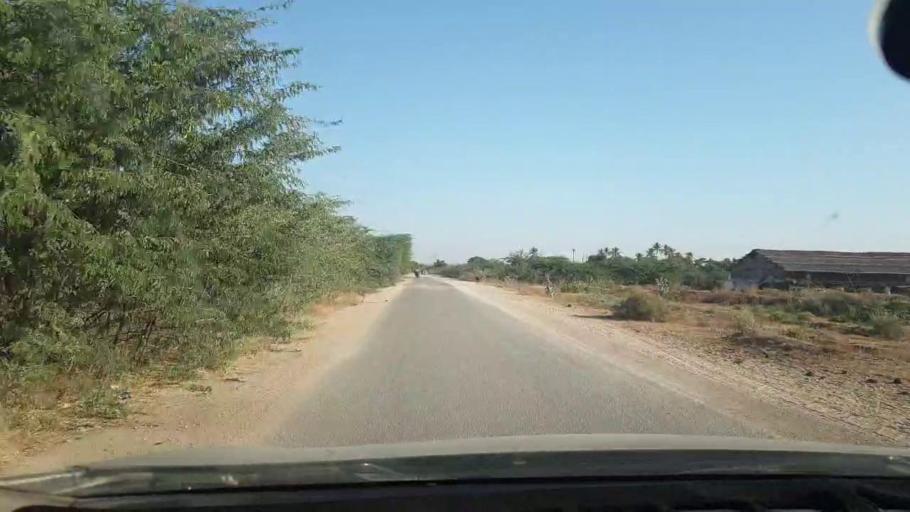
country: PK
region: Sindh
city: Malir Cantonment
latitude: 25.1716
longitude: 67.2013
